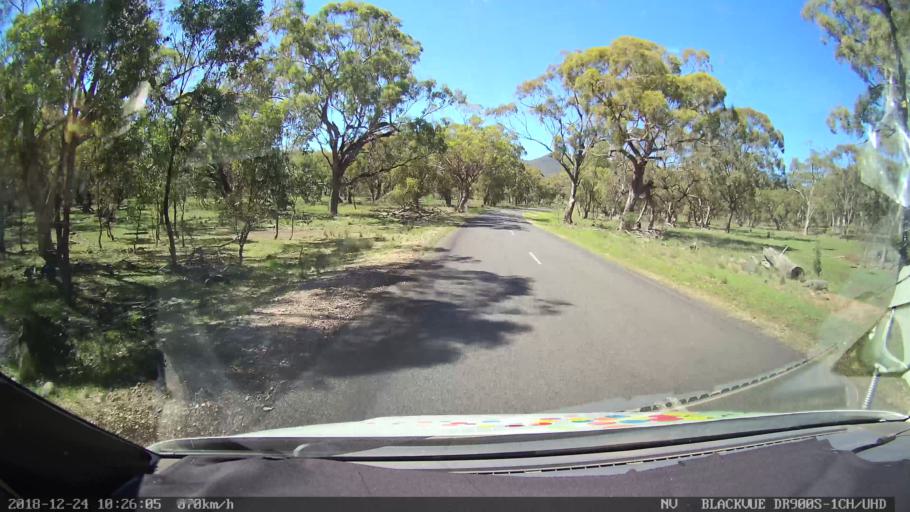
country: AU
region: New South Wales
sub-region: Liverpool Plains
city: Quirindi
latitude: -31.8059
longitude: 150.5279
